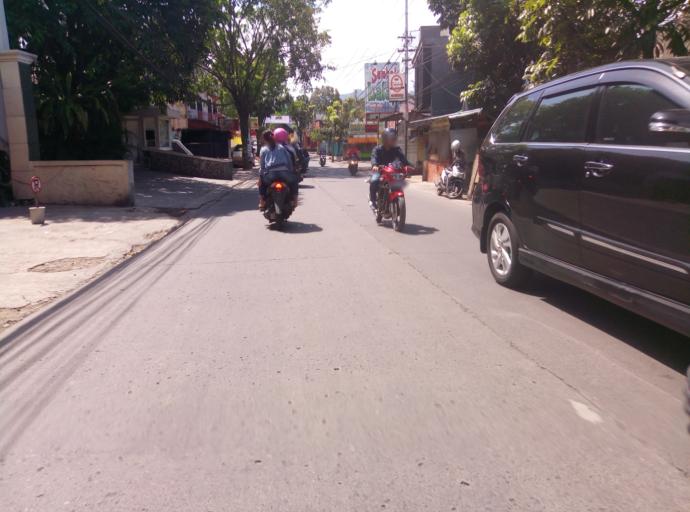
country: ID
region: West Java
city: Bandung
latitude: -6.8986
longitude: 107.6436
